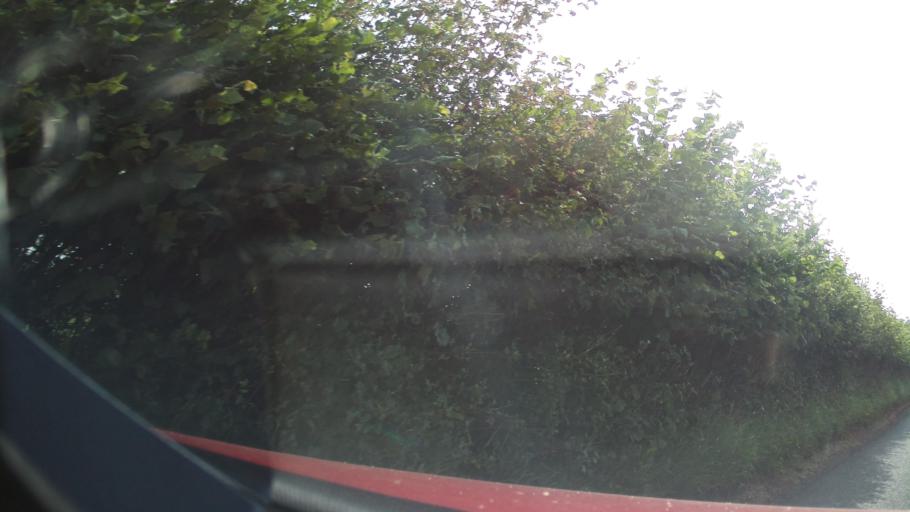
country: GB
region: England
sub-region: Bath and North East Somerset
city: East Harptree
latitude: 51.3070
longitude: -2.6258
